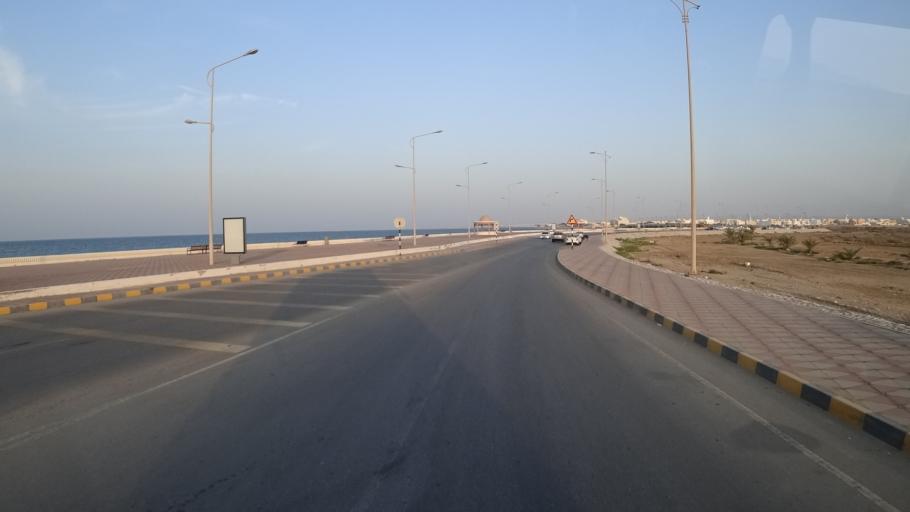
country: OM
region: Ash Sharqiyah
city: Sur
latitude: 22.6023
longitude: 59.4837
